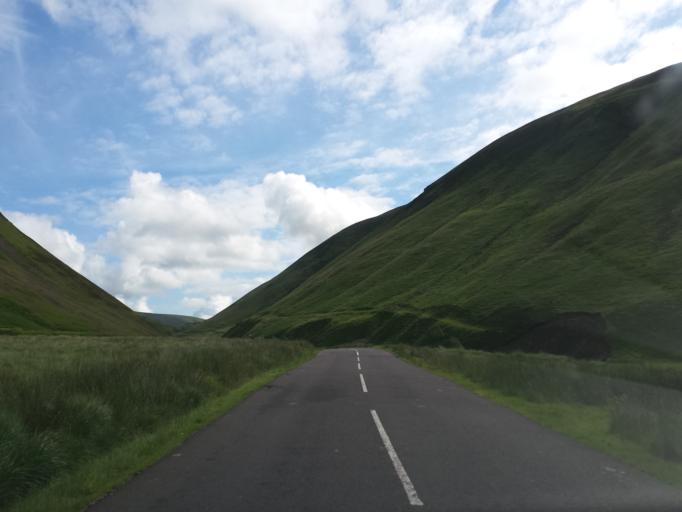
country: GB
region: Scotland
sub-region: Dumfries and Galloway
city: Moffat
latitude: 55.4163
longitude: -3.2890
